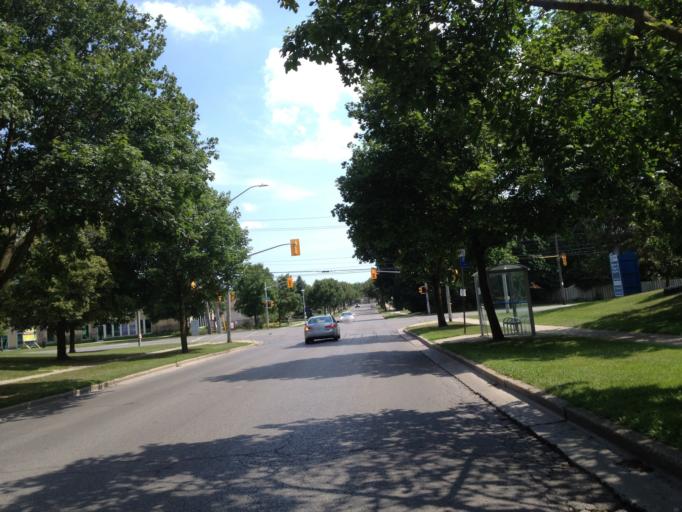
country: CA
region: Ontario
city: London
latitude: 43.0040
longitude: -81.3163
